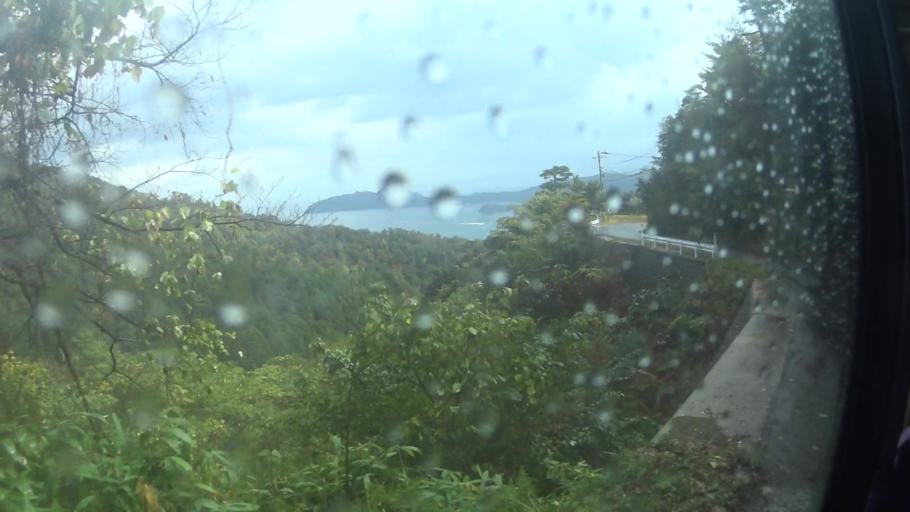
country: JP
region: Kyoto
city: Miyazu
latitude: 35.5876
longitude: 135.1818
